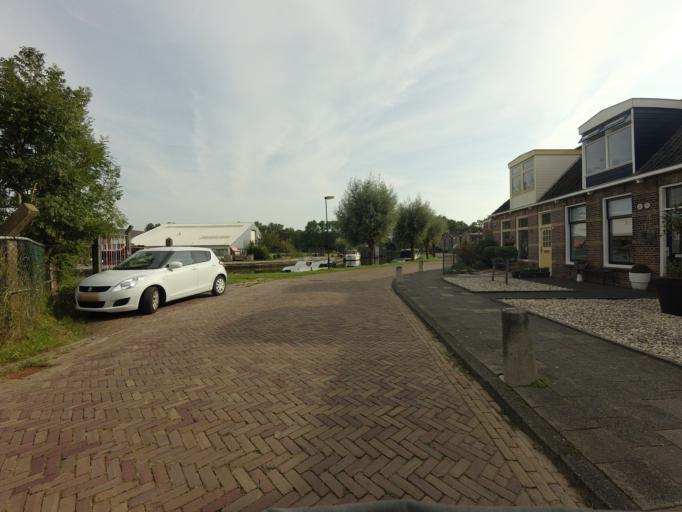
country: NL
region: Friesland
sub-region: Sudwest Fryslan
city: Bolsward
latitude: 53.0602
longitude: 5.5169
